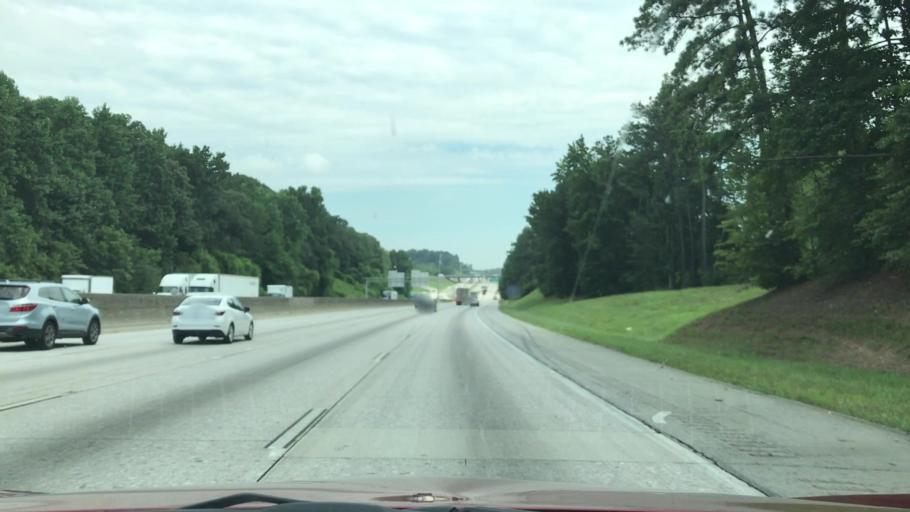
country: US
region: Georgia
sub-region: Fulton County
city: College Park
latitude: 33.6484
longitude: -84.4974
